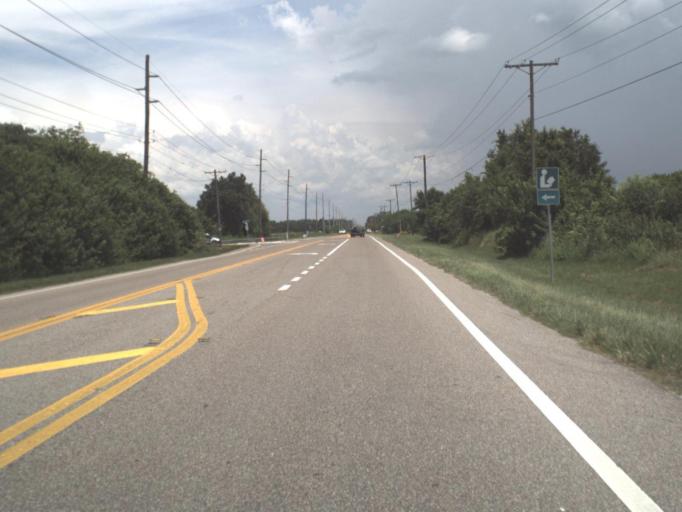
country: US
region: Florida
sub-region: Hillsborough County
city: Sun City Center
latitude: 27.7395
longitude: -82.3352
